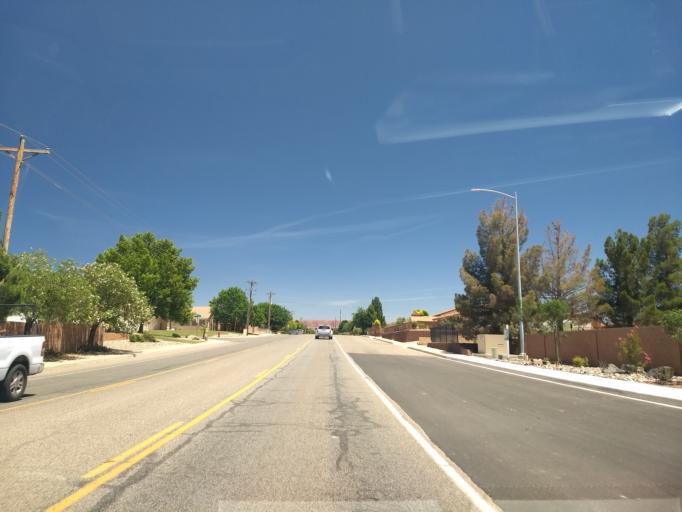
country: US
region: Utah
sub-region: Washington County
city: Saint George
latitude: 37.0668
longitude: -113.5444
